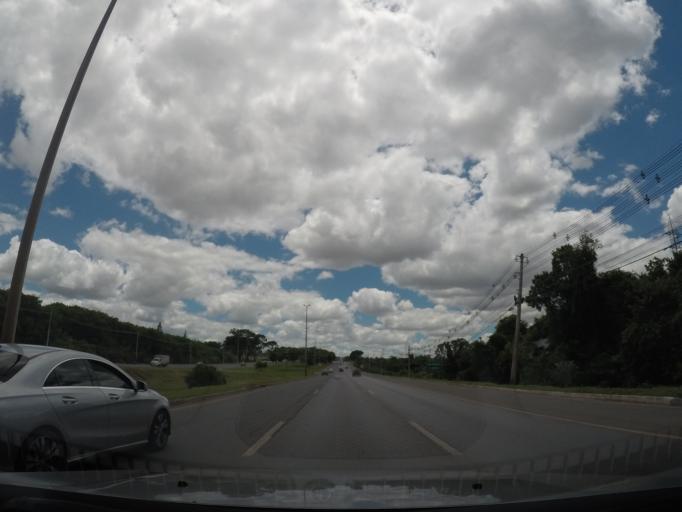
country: BR
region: Federal District
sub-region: Brasilia
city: Brasilia
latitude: -15.7291
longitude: -47.9102
